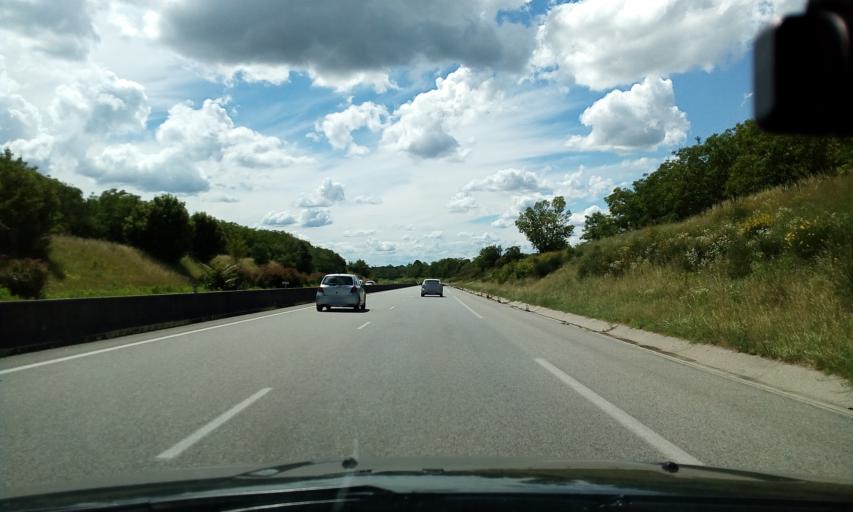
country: FR
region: Rhone-Alpes
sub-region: Departement de l'Isere
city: Chatte
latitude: 45.1242
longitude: 5.2893
